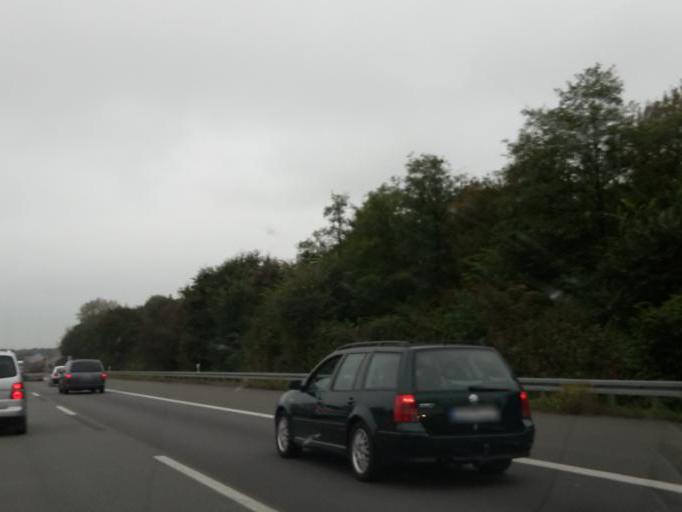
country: DE
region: North Rhine-Westphalia
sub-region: Regierungsbezirk Munster
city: Ladbergen
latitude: 52.1185
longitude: 7.7062
